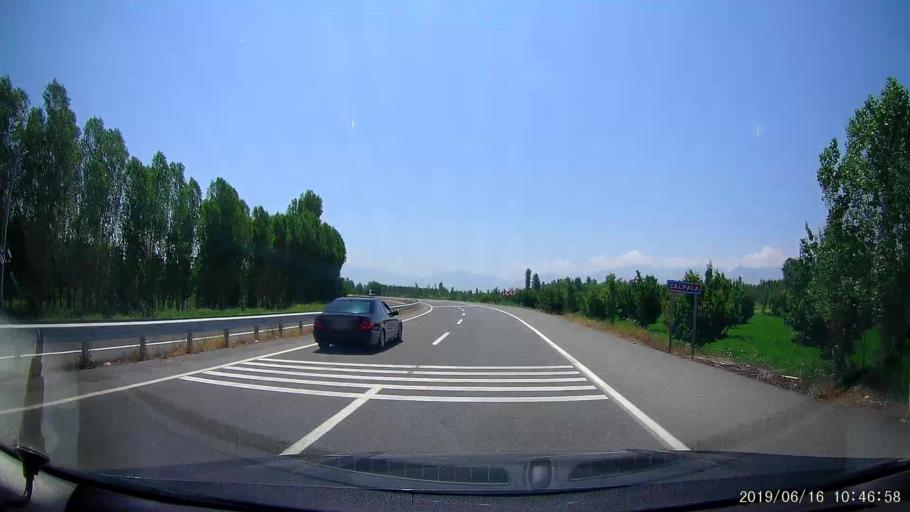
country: AM
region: Armavir
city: Shenavan
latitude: 40.0163
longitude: 43.8828
